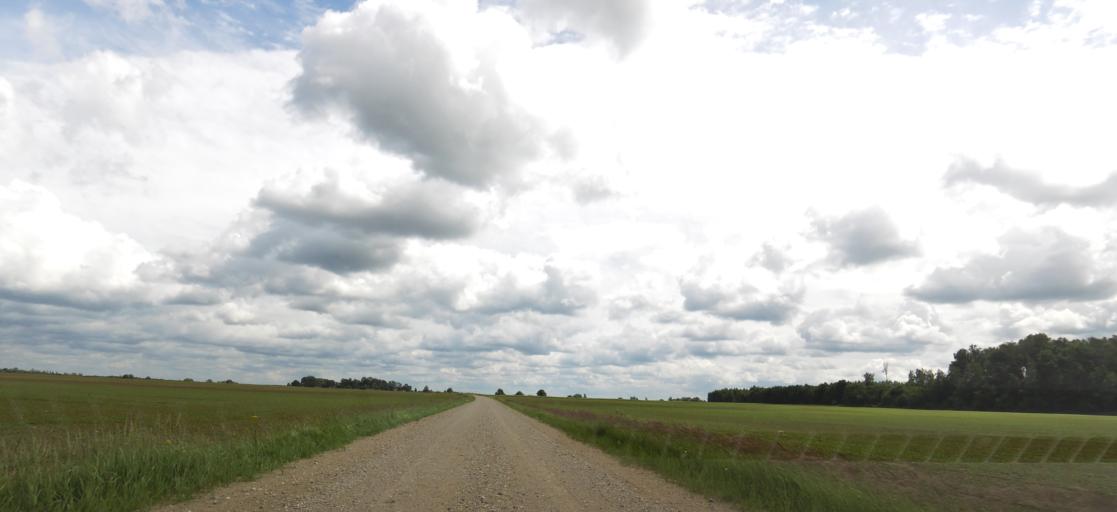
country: LT
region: Panevezys
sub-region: Birzai
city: Birzai
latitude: 56.3153
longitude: 24.7534
